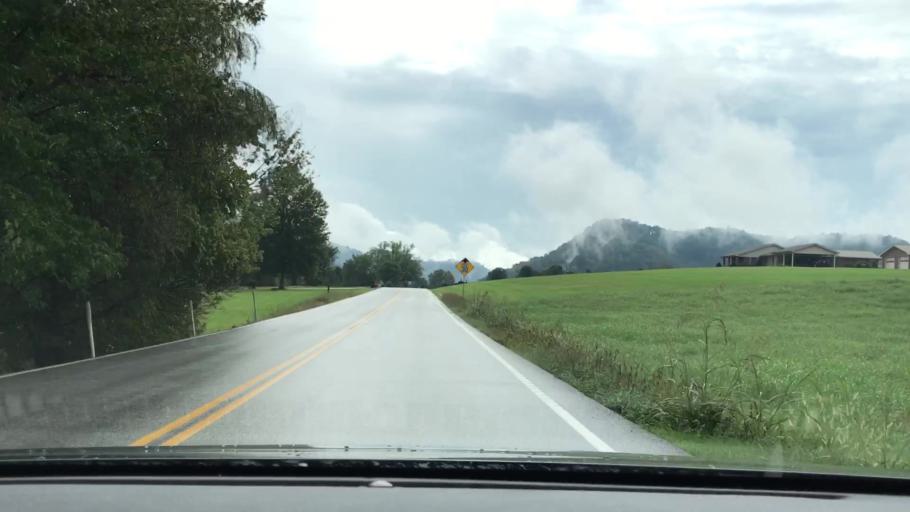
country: US
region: Tennessee
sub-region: Smith County
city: Carthage
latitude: 36.3897
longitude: -85.9480
